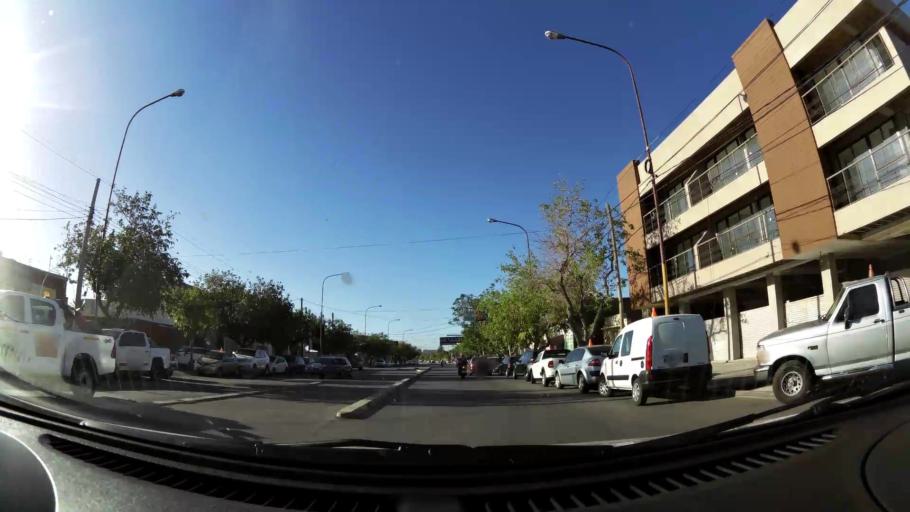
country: AR
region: San Juan
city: San Juan
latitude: -31.5480
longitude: -68.5206
